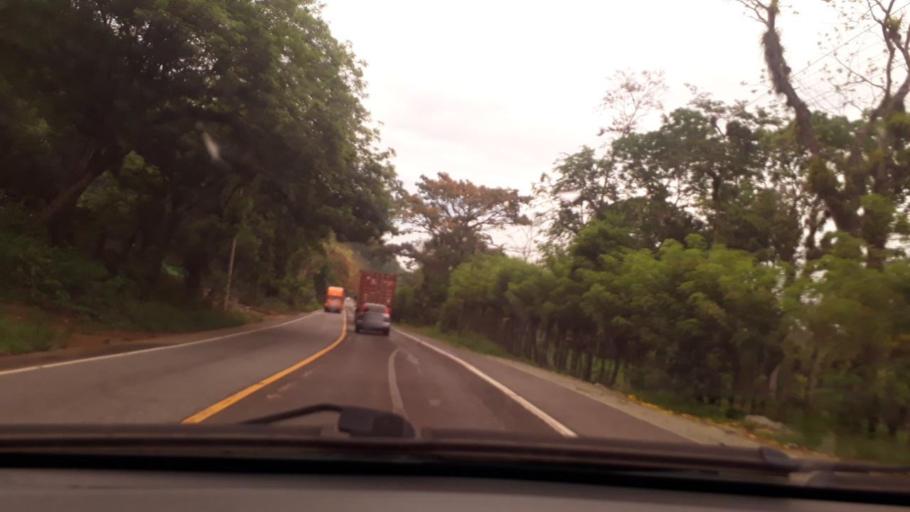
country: GT
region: Izabal
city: Morales
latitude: 15.5438
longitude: -88.7072
